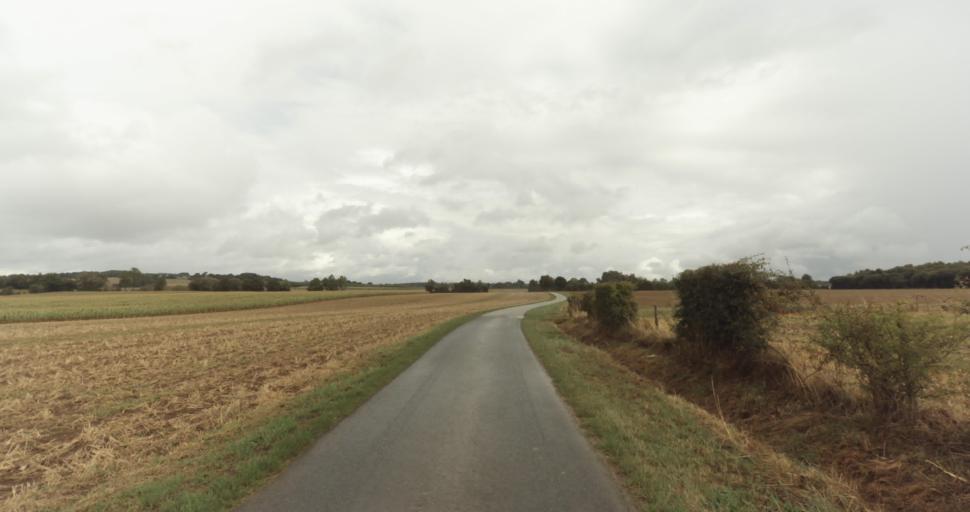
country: FR
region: Lower Normandy
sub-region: Departement de l'Orne
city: Sainte-Gauburge-Sainte-Colombe
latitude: 48.6858
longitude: 0.3974
